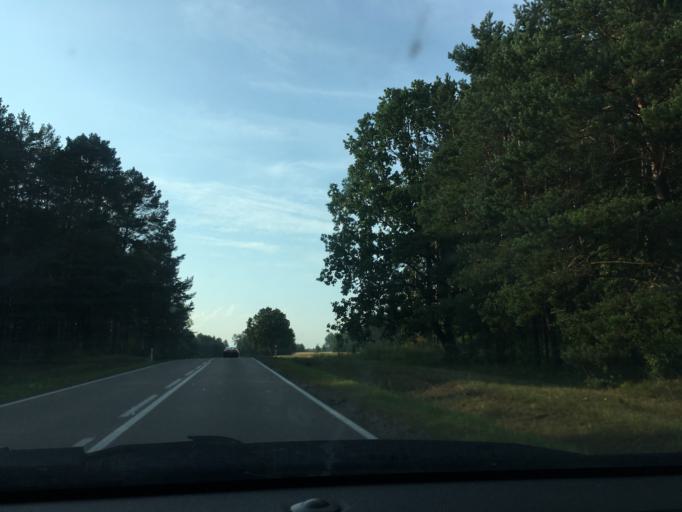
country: PL
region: Podlasie
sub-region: Powiat moniecki
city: Knyszyn
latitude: 53.2815
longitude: 22.9513
